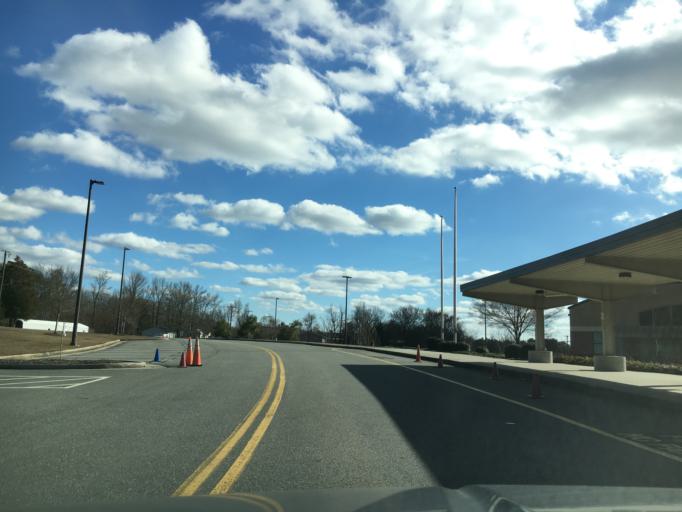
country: US
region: Virginia
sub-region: Halifax County
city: South Boston
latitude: 36.7192
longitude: -78.8894
